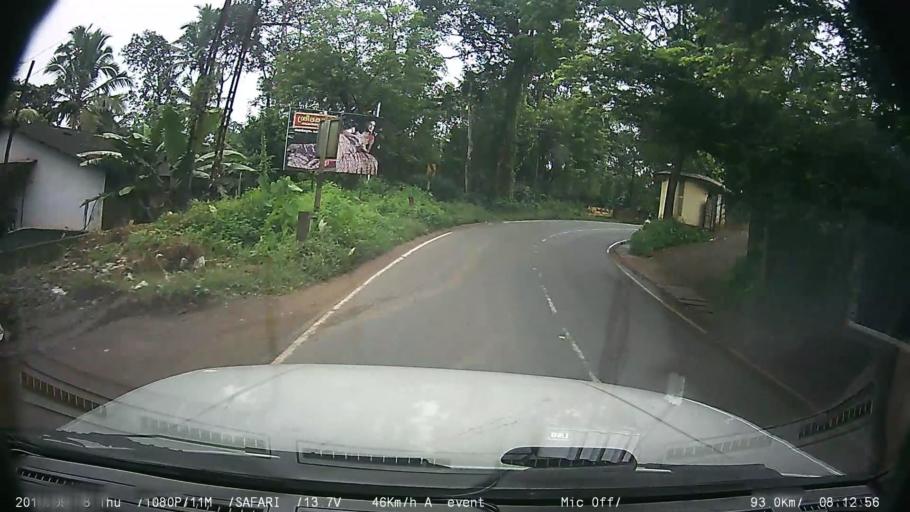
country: IN
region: Kerala
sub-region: Kottayam
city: Kottayam
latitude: 9.6124
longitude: 76.6039
